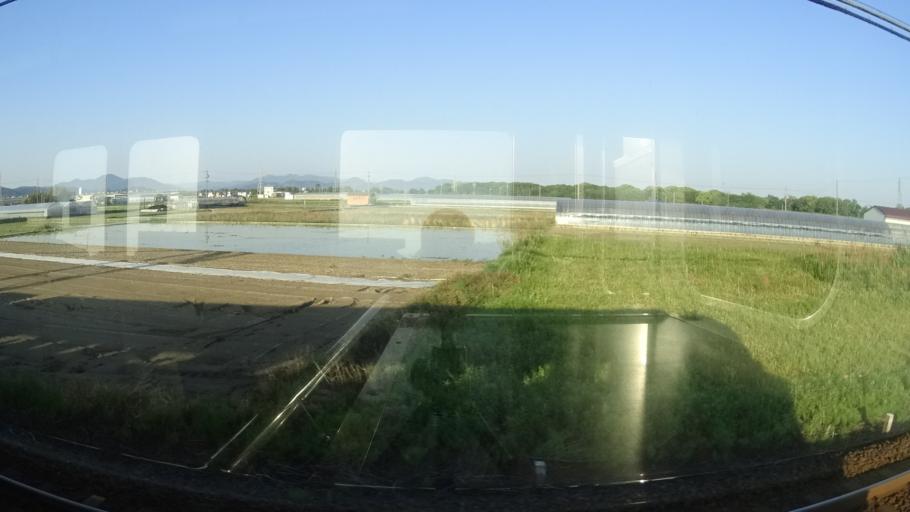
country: JP
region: Mie
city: Ise
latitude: 34.5057
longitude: 136.6938
